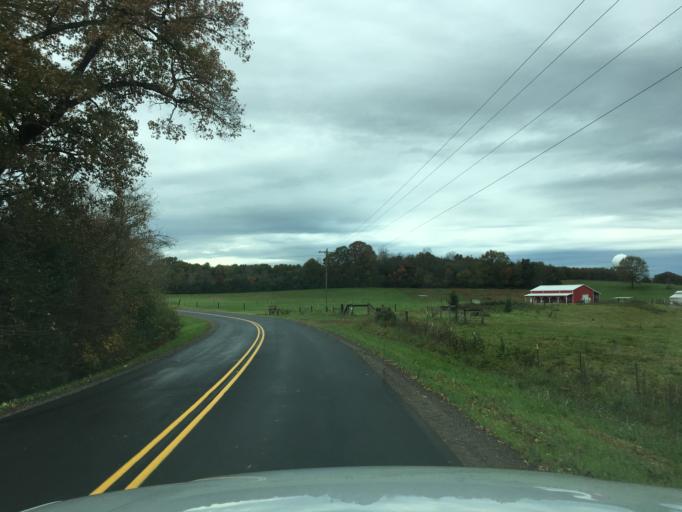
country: US
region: North Carolina
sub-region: Catawba County
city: Maiden
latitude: 35.6086
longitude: -81.2310
